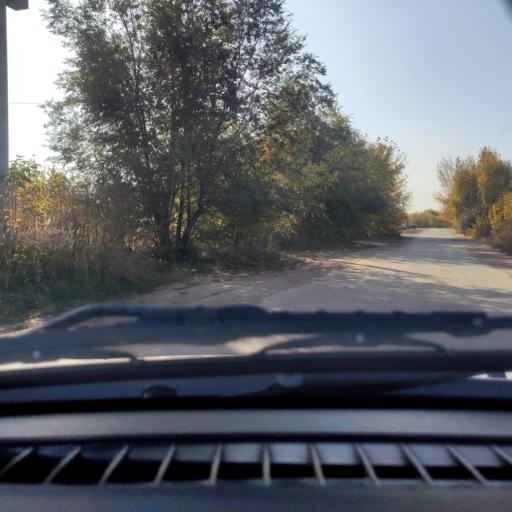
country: RU
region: Samara
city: Tol'yatti
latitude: 53.5463
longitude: 49.4328
